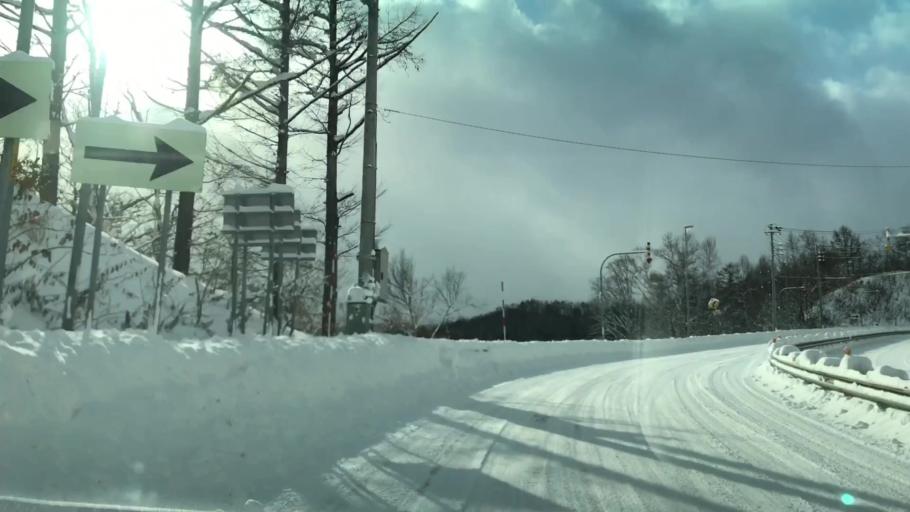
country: JP
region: Hokkaido
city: Yoichi
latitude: 43.2906
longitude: 140.5858
